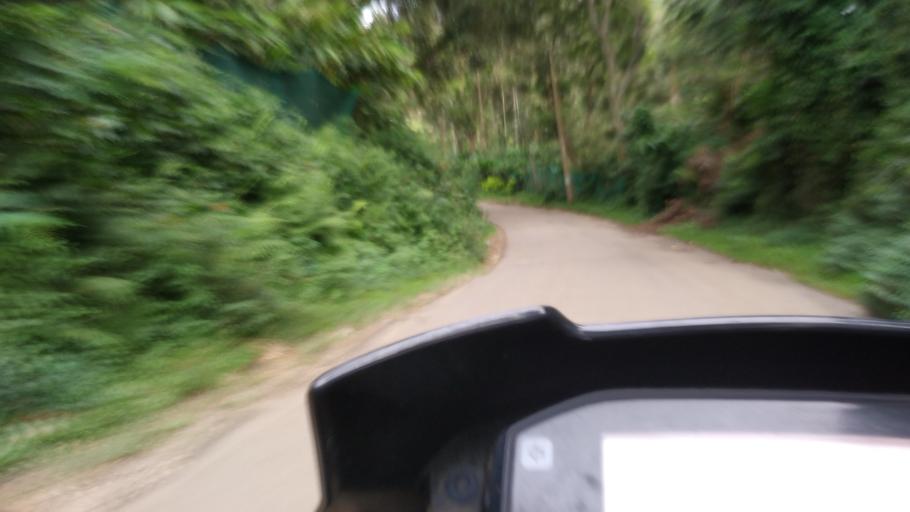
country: IN
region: Tamil Nadu
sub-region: Theni
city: Bodinayakkanur
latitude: 10.0251
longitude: 77.2346
